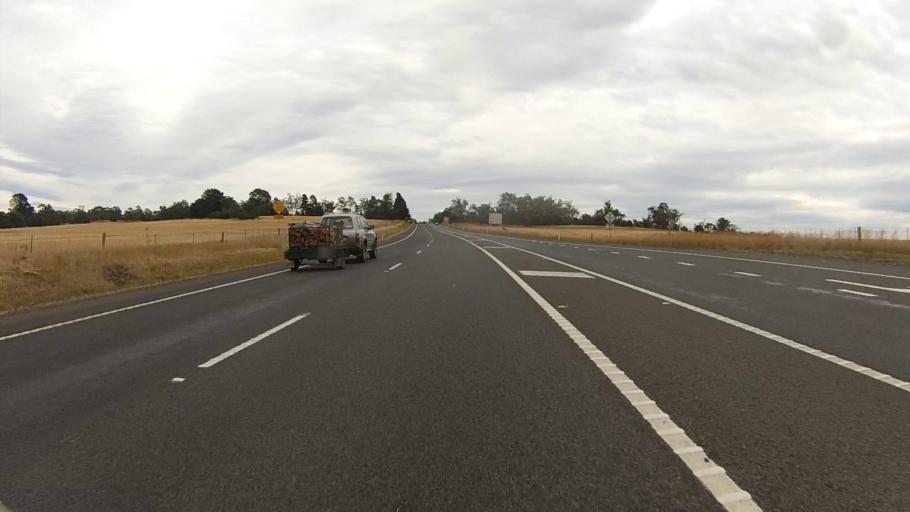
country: AU
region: Tasmania
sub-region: Northern Midlands
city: Evandale
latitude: -41.8348
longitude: 147.4466
